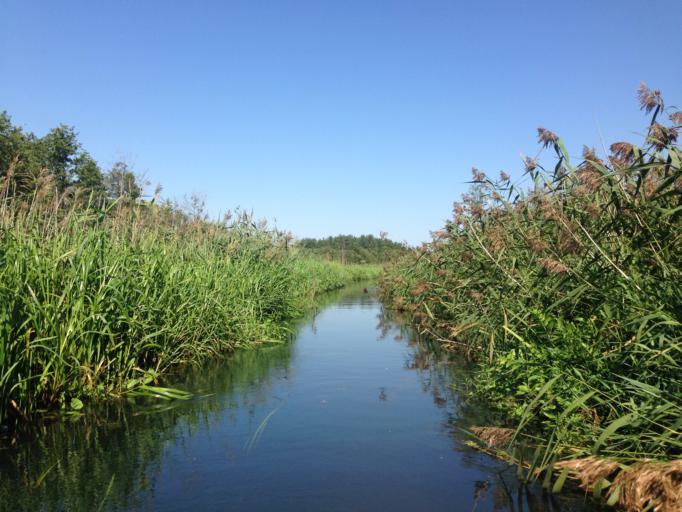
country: PL
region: Kujawsko-Pomorskie
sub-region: Powiat brodnicki
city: Bartniczka
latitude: 53.2560
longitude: 19.6024
